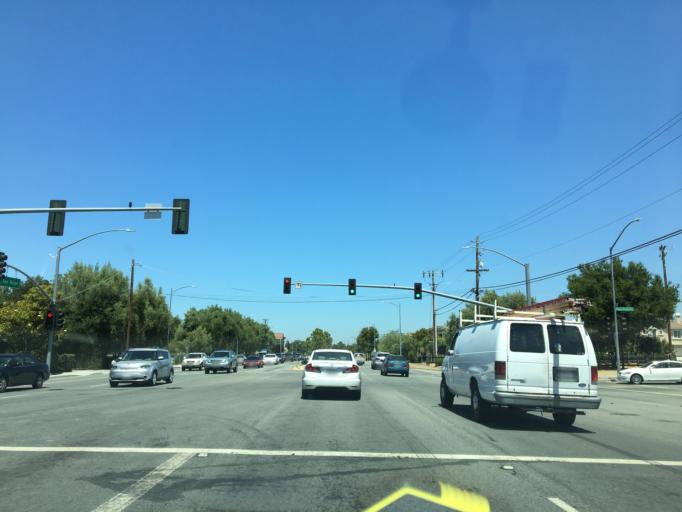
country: US
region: California
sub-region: Santa Clara County
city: Seven Trees
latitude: 37.3022
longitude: -121.7743
